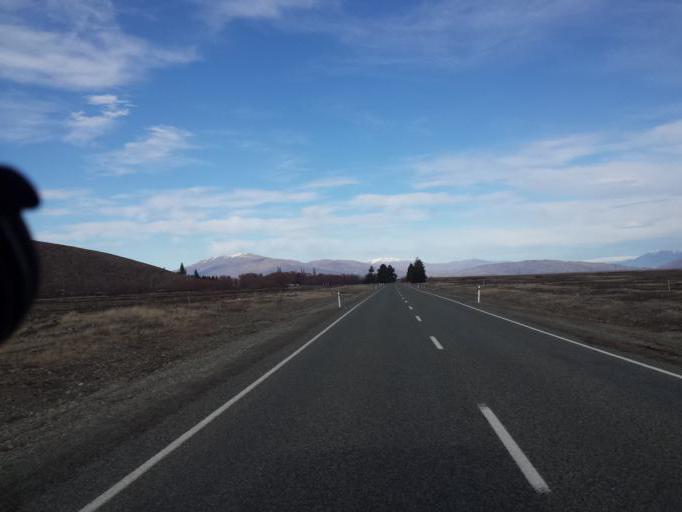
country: NZ
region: Canterbury
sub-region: Timaru District
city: Pleasant Point
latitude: -44.0535
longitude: 170.5026
